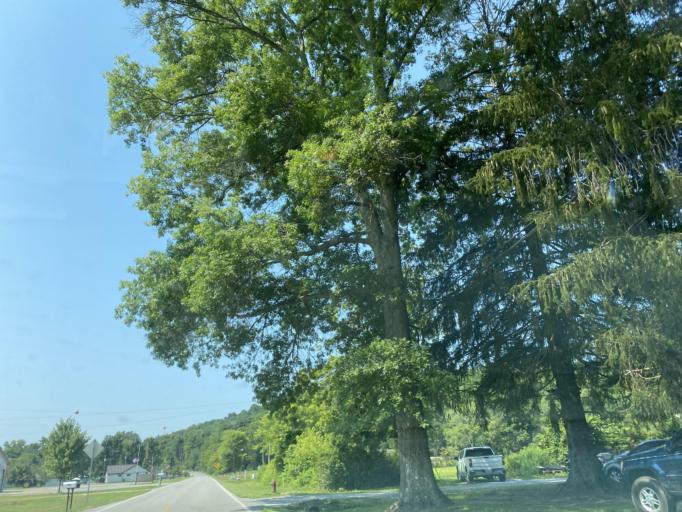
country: US
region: Kentucky
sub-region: Campbell County
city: Claryville
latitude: 38.8654
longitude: -84.4592
